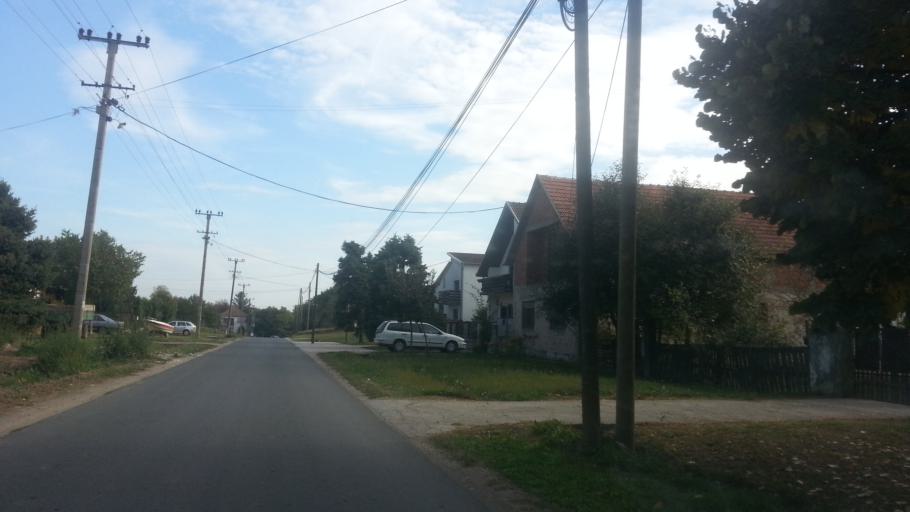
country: RS
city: Belegis
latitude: 45.0154
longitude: 20.3229
